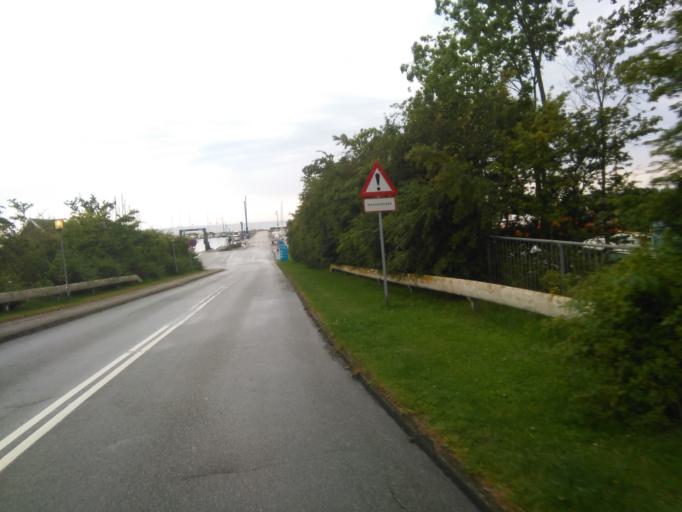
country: DK
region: Central Jutland
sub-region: Arhus Kommune
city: Hjortshoj
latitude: 56.2101
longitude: 10.2857
